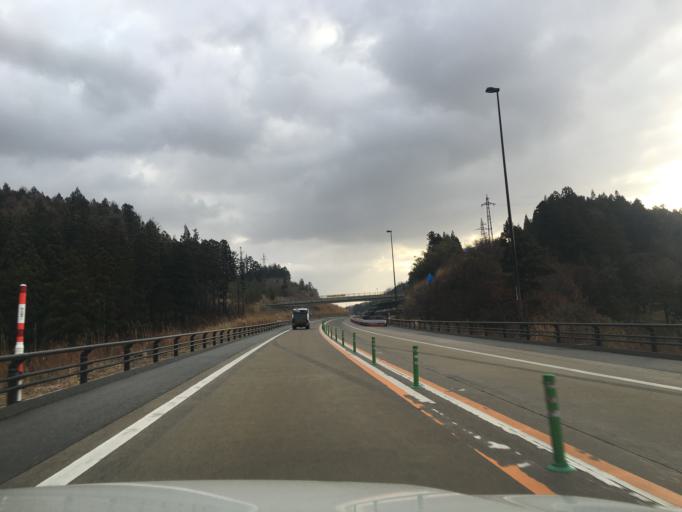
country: JP
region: Yamagata
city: Tsuruoka
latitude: 38.6963
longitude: 139.6989
